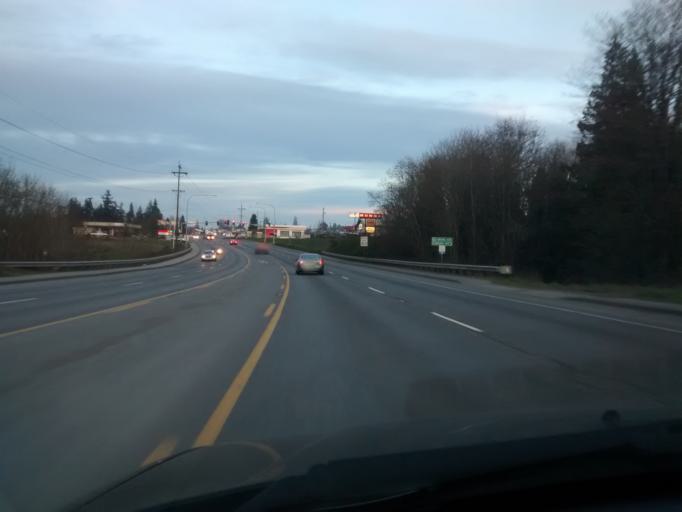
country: US
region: Washington
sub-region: Clallam County
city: Port Angeles East
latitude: 48.1044
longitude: -123.3839
